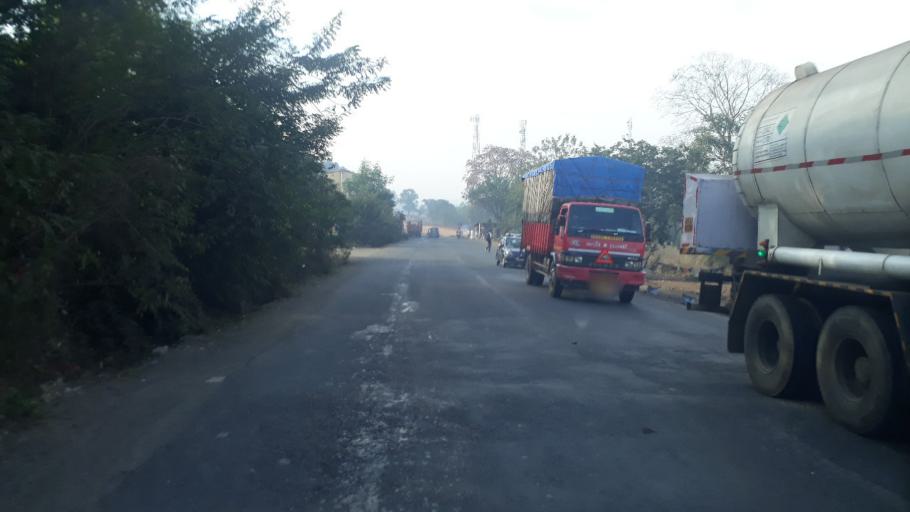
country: IN
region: Maharashtra
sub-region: Raigarh
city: Pen
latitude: 18.8574
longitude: 73.0996
